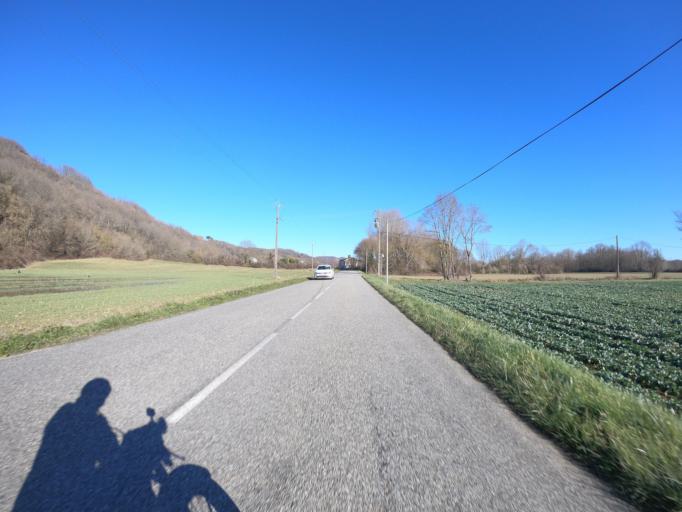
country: FR
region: Midi-Pyrenees
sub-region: Departement de l'Ariege
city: Mirepoix
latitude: 43.0884
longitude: 1.8372
